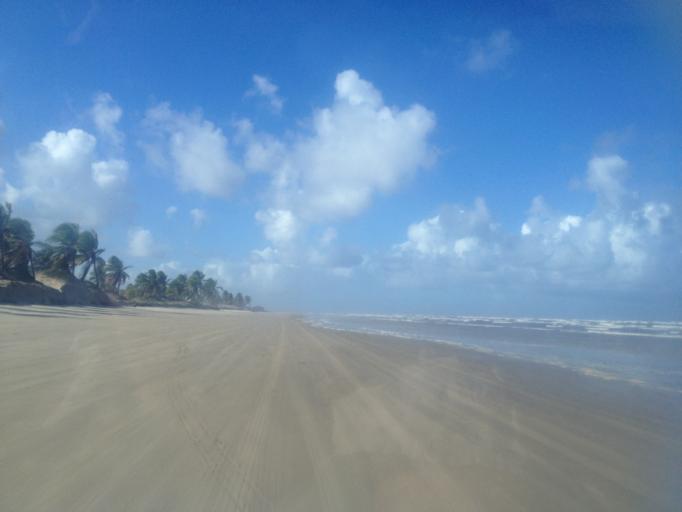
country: BR
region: Sergipe
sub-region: Indiaroba
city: Indiaroba
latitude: -11.4711
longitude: -37.3578
